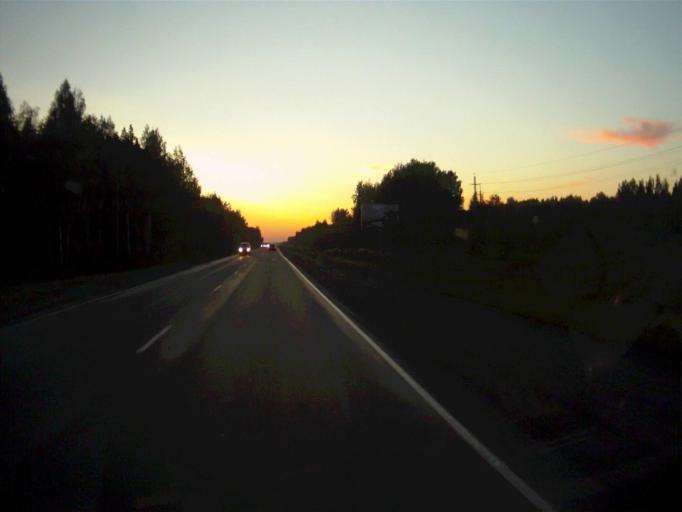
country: RU
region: Chelyabinsk
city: Poletayevo
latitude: 55.2095
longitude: 61.0876
